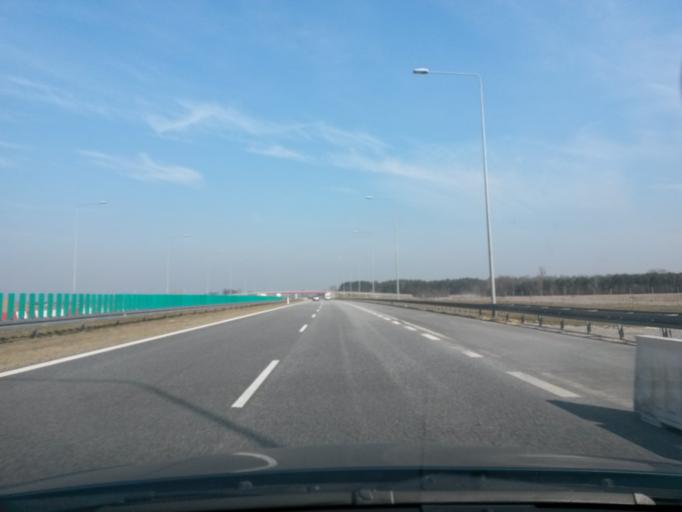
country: PL
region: Lodz Voivodeship
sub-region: Powiat kutnowski
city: Krzyzanow
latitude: 52.1867
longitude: 19.4878
